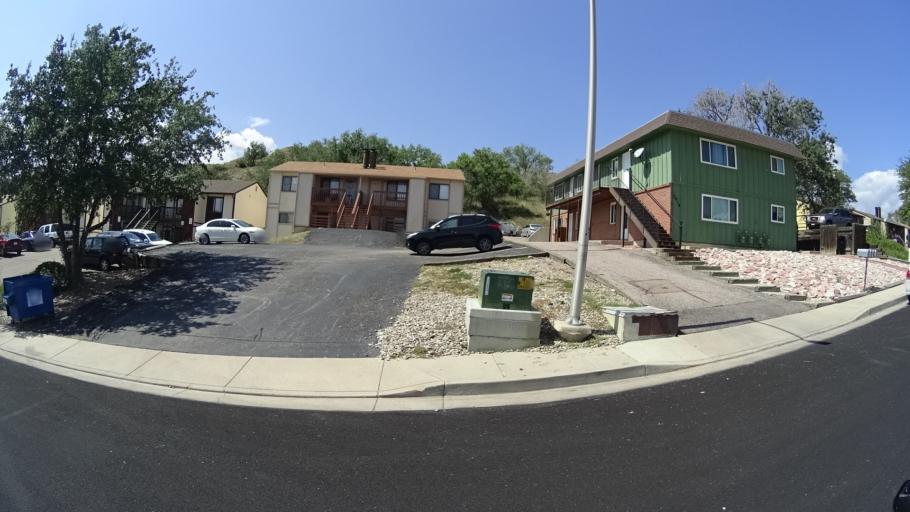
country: US
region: Colorado
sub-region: El Paso County
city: Colorado Springs
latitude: 38.8744
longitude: -104.8396
